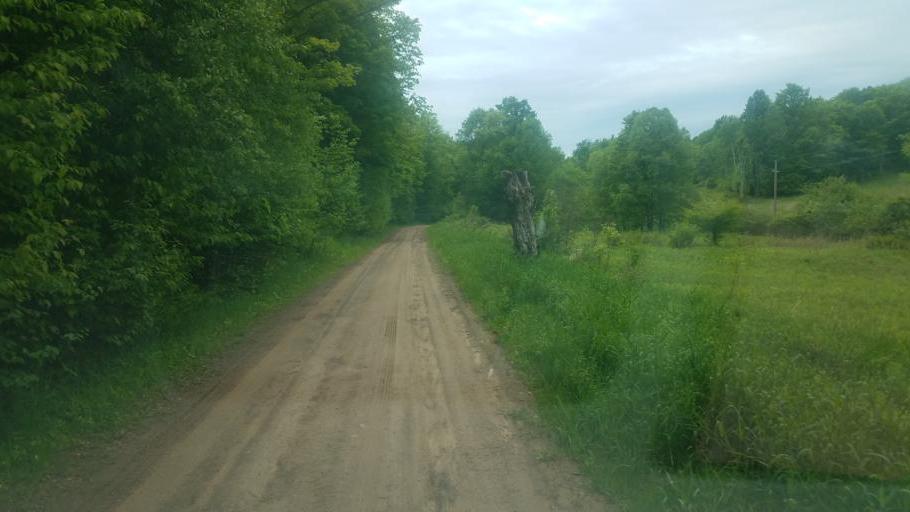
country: US
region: Pennsylvania
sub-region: Tioga County
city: Westfield
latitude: 41.9263
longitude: -77.6884
